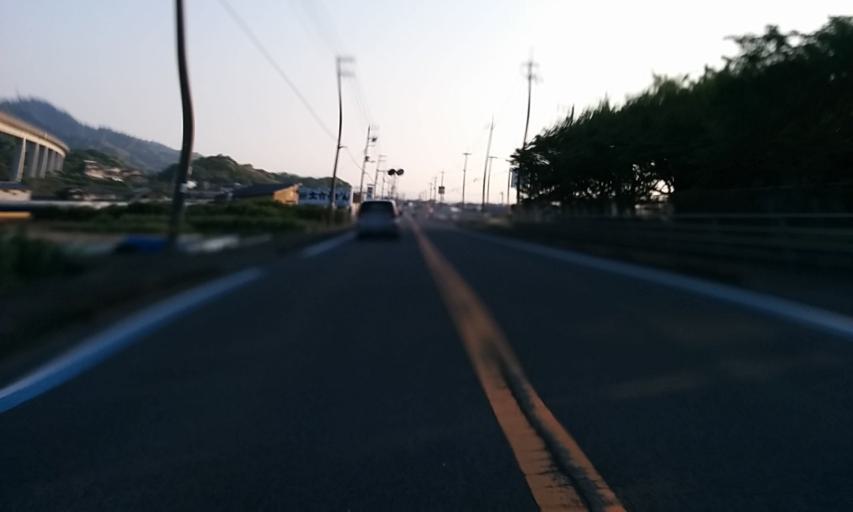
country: JP
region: Ehime
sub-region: Shikoku-chuo Shi
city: Matsuyama
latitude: 33.7884
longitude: 132.7683
